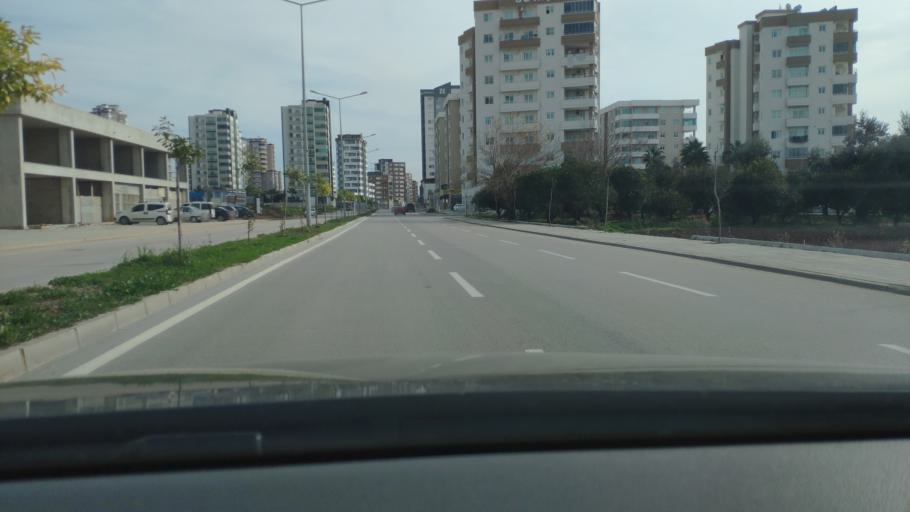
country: TR
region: Adana
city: Seyhan
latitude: 37.0161
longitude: 35.2610
